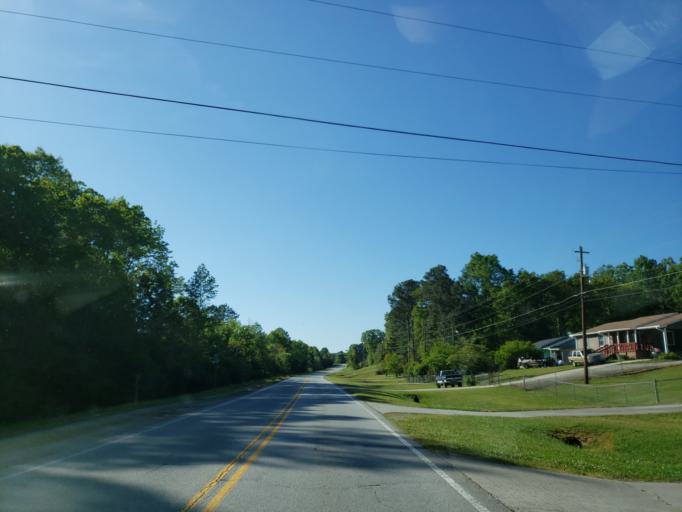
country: US
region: Georgia
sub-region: Polk County
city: Cedartown
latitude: 33.9970
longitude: -85.2344
